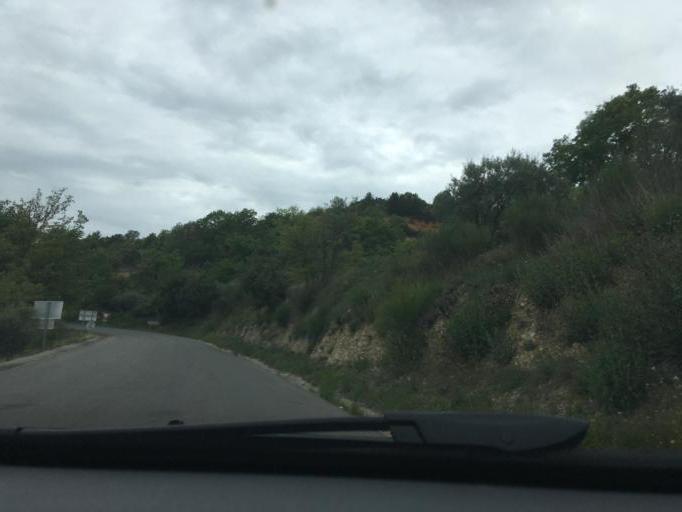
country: FR
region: Provence-Alpes-Cote d'Azur
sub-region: Departement des Alpes-de-Haute-Provence
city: Riez
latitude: 43.7601
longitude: 6.1494
